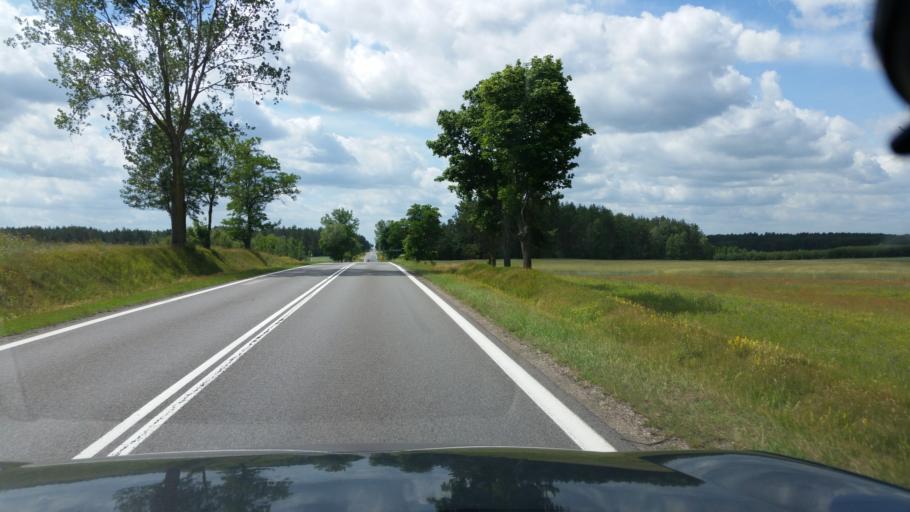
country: PL
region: Podlasie
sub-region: Powiat kolnenski
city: Stawiski
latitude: 53.4517
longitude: 22.1878
